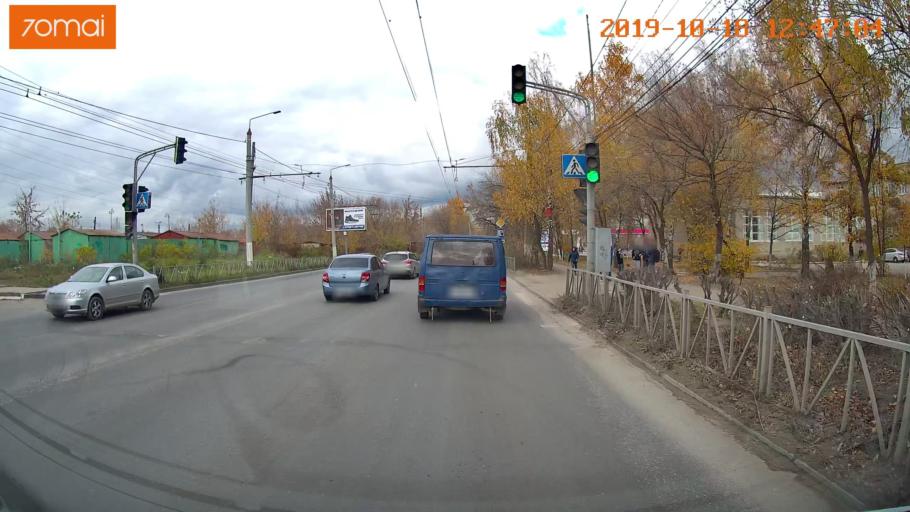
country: RU
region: Rjazan
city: Ryazan'
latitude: 54.6563
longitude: 39.6638
